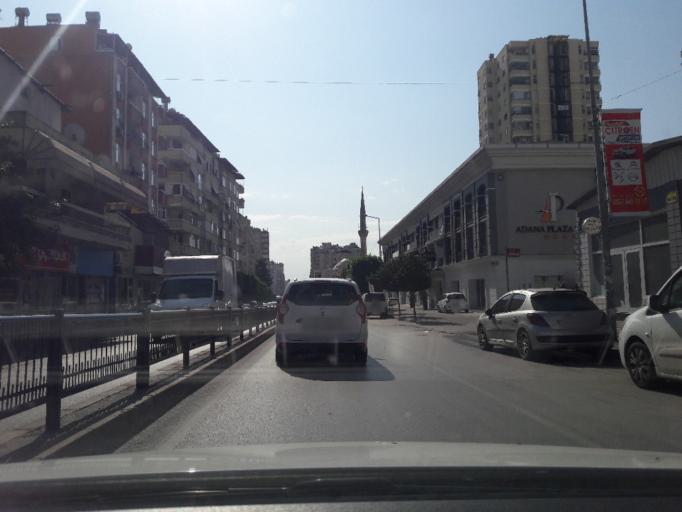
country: TR
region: Adana
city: Adana
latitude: 37.0133
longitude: 35.3226
